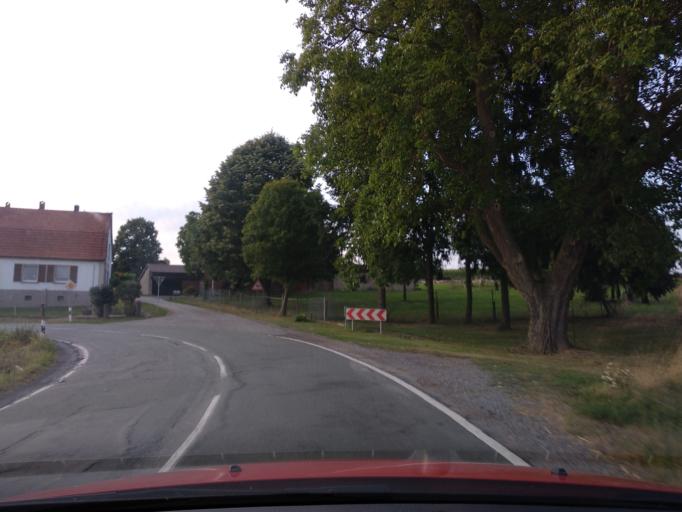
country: DE
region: North Rhine-Westphalia
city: Beverungen
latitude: 51.6748
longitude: 9.2940
